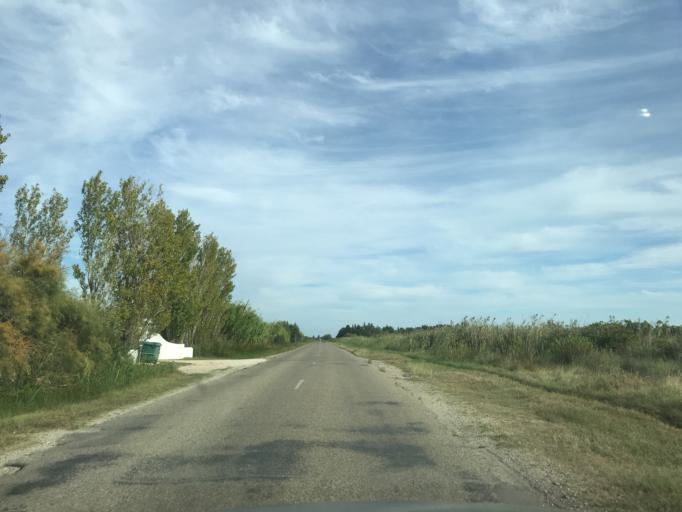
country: FR
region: Provence-Alpes-Cote d'Azur
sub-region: Departement des Bouches-du-Rhone
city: Saintes-Maries-de-la-Mer
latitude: 43.5250
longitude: 4.3786
